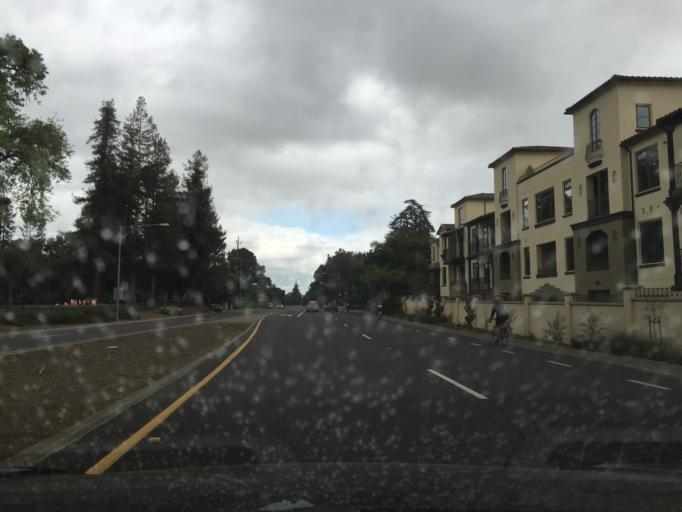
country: US
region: California
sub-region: Santa Clara County
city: Los Altos
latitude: 37.3802
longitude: -122.1203
